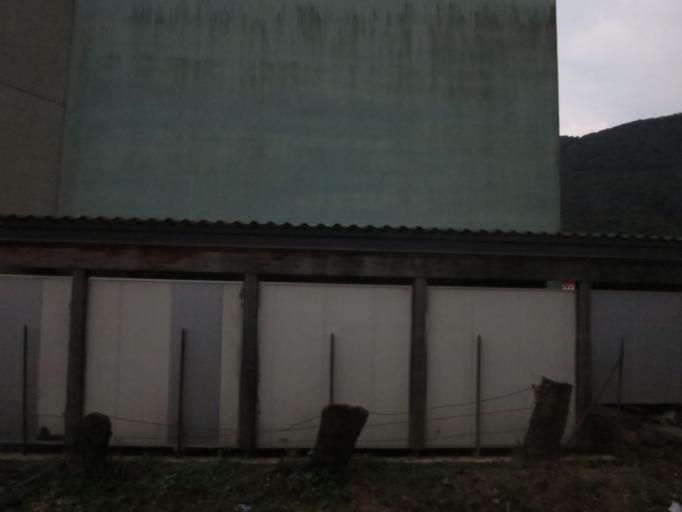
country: CH
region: Ticino
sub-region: Lugano District
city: Gravesano
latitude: 46.0464
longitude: 8.9260
